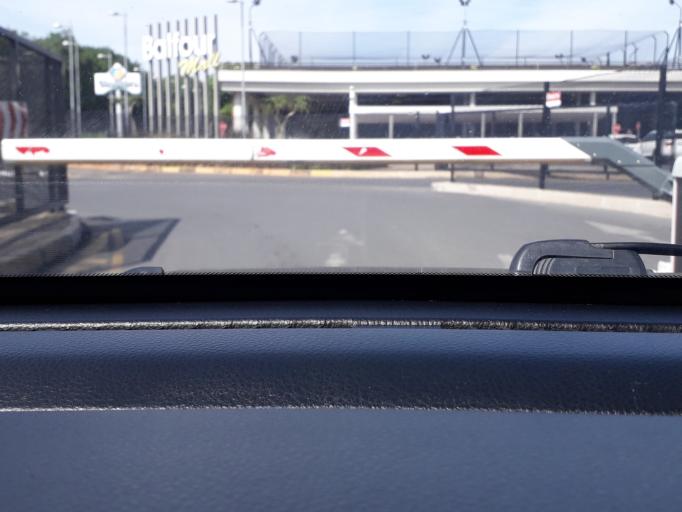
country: ZA
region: Gauteng
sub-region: City of Johannesburg Metropolitan Municipality
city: Johannesburg
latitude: -26.1367
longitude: 28.0912
